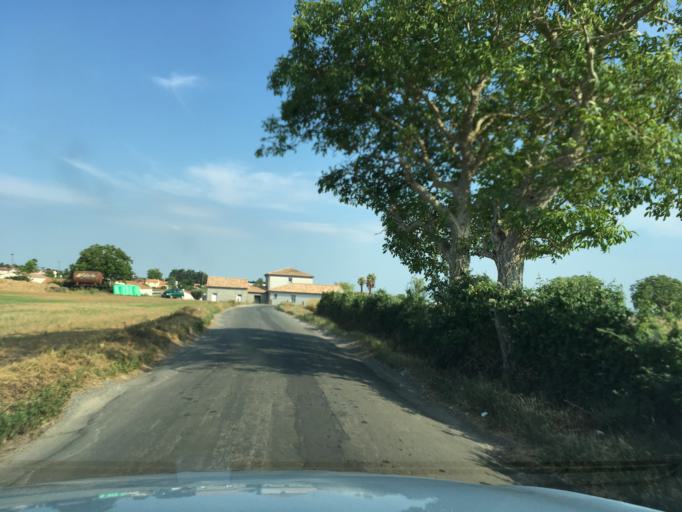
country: FR
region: Poitou-Charentes
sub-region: Departement des Deux-Sevres
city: Niort
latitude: 46.3424
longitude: -0.4249
